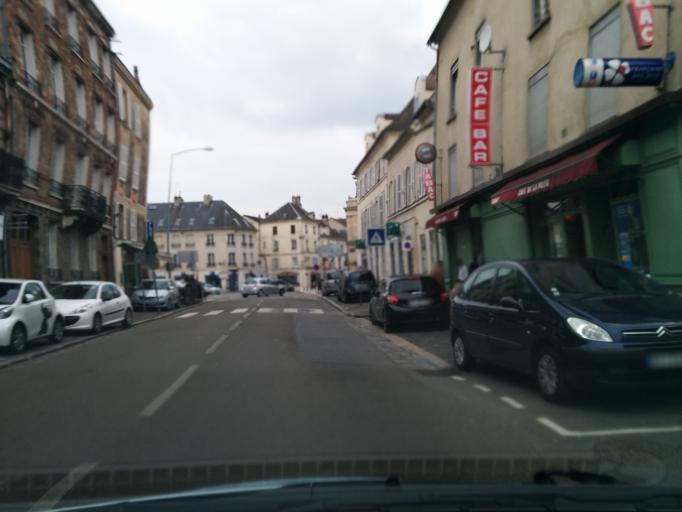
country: FR
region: Ile-de-France
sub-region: Departement des Yvelines
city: Meulan-en-Yvelines
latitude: 49.0050
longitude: 1.9111
